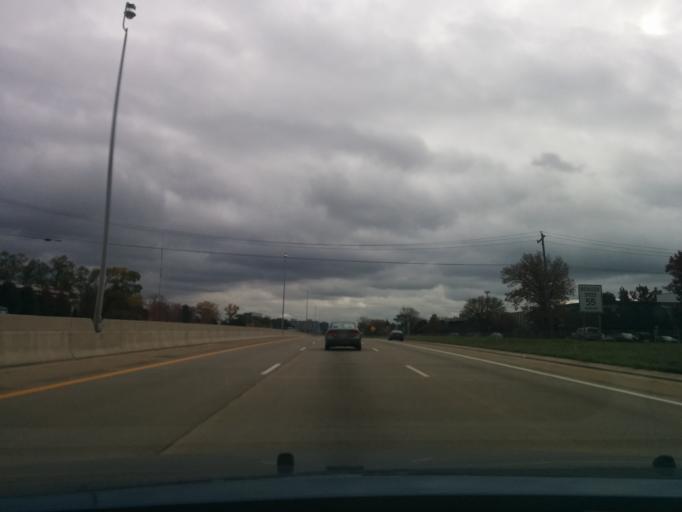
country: US
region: Michigan
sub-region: Oakland County
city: Southfield
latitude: 42.4687
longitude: -83.2362
